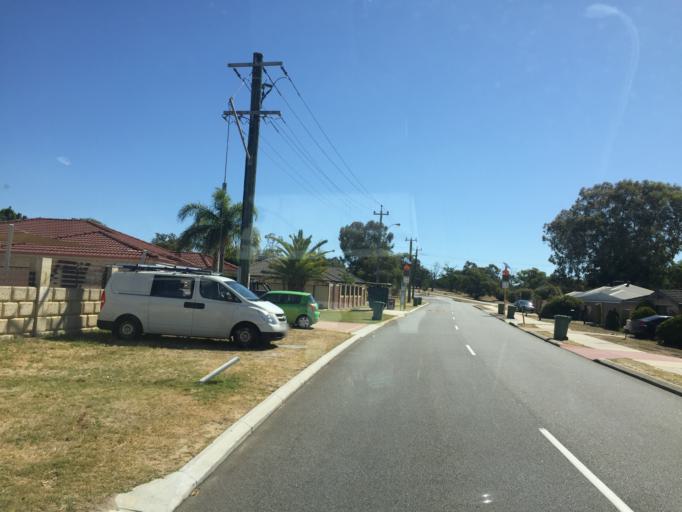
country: AU
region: Western Australia
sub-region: Belmont
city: Redcliffe
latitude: -31.9352
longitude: 115.9476
